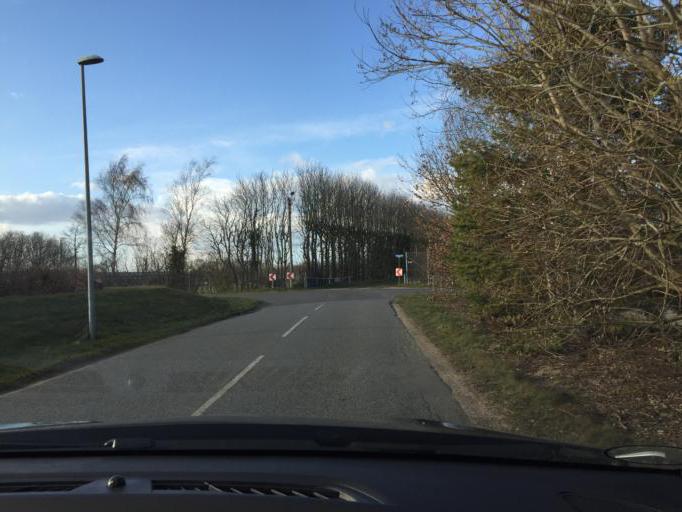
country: DK
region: South Denmark
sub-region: Kerteminde Kommune
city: Langeskov
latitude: 55.3546
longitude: 10.6030
